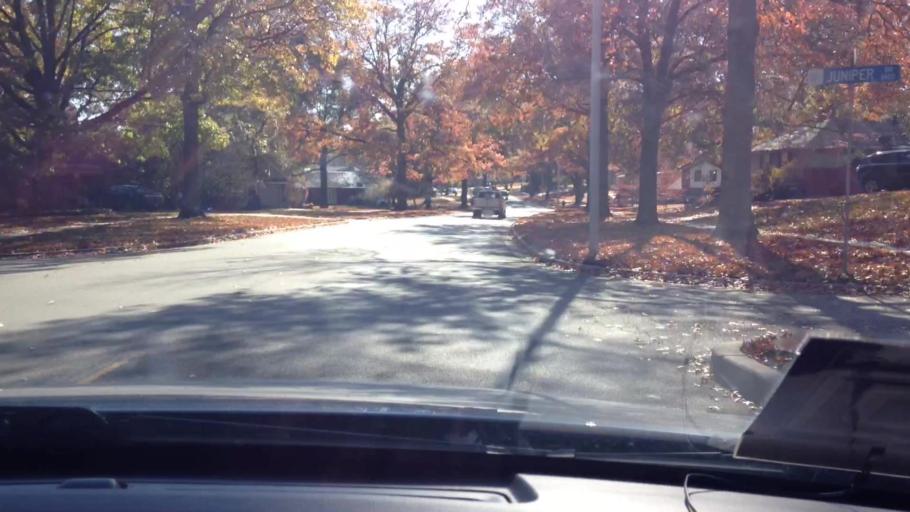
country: US
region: Kansas
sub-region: Johnson County
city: Prairie Village
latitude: 38.9809
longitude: -94.6392
